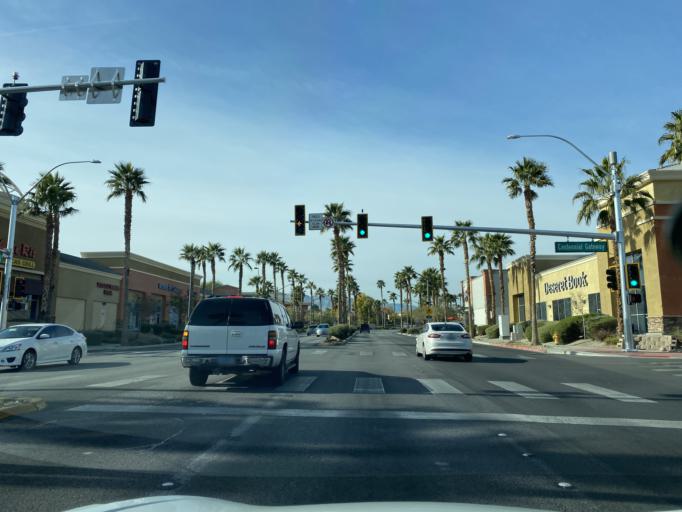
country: US
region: Nevada
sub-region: Clark County
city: Las Vegas
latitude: 36.2652
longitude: -115.2584
